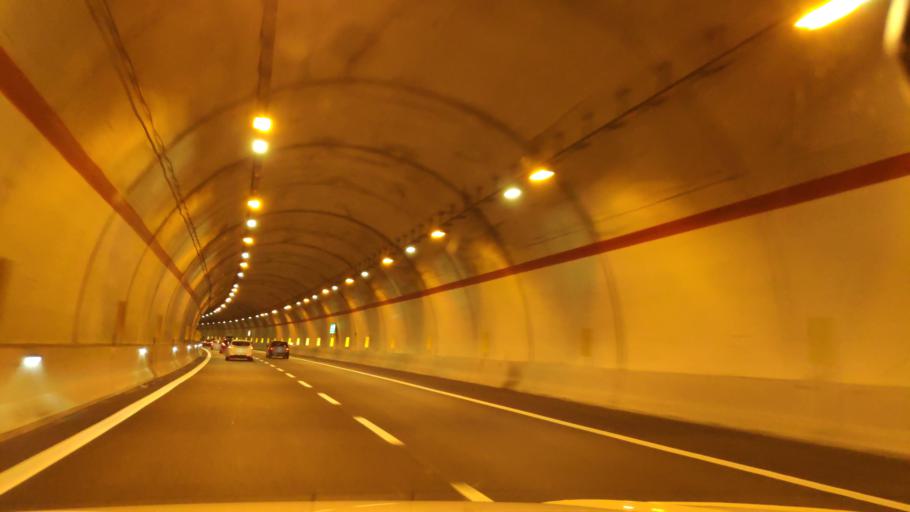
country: IT
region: Calabria
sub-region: Provincia di Cosenza
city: Mormanno
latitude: 39.8870
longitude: 16.0501
